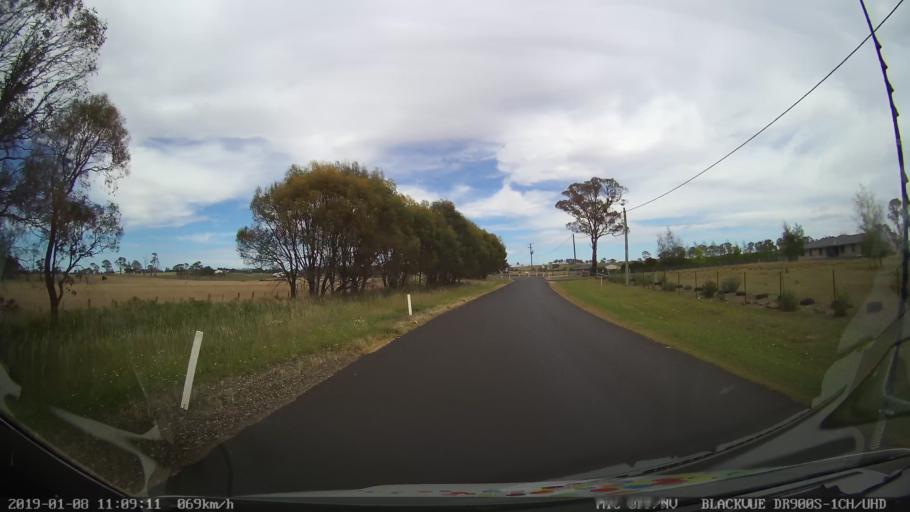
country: AU
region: New South Wales
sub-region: Guyra
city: Guyra
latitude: -30.2248
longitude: 151.6503
